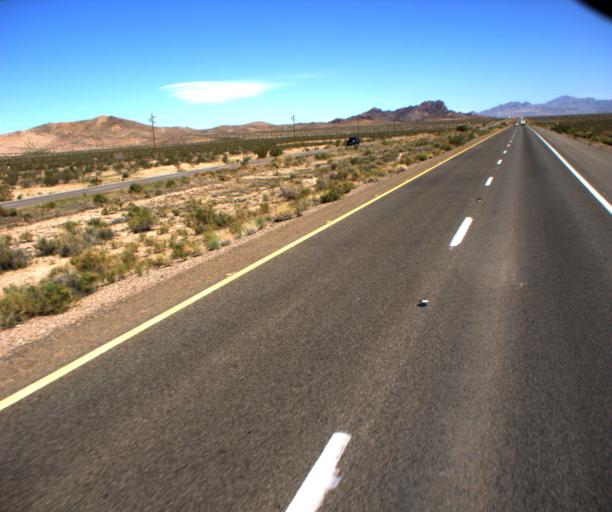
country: US
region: Arizona
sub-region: Mohave County
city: Dolan Springs
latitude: 35.7356
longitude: -114.4936
